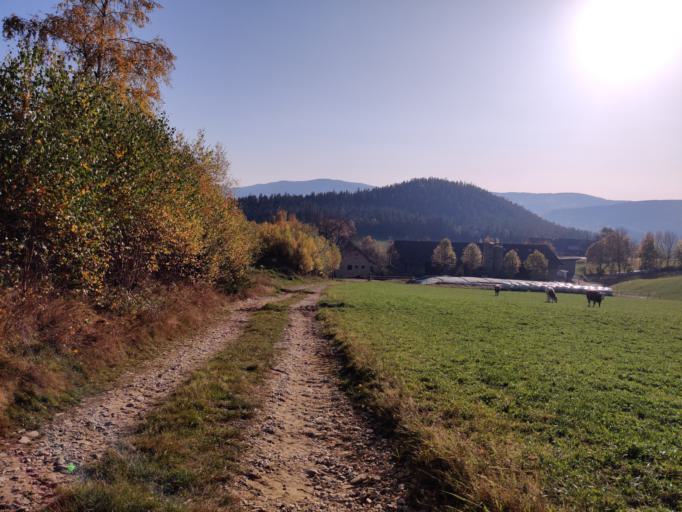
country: AT
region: Styria
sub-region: Politischer Bezirk Hartberg-Fuerstenfeld
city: Sankt Jakob im Walde
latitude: 47.4675
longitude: 15.8101
